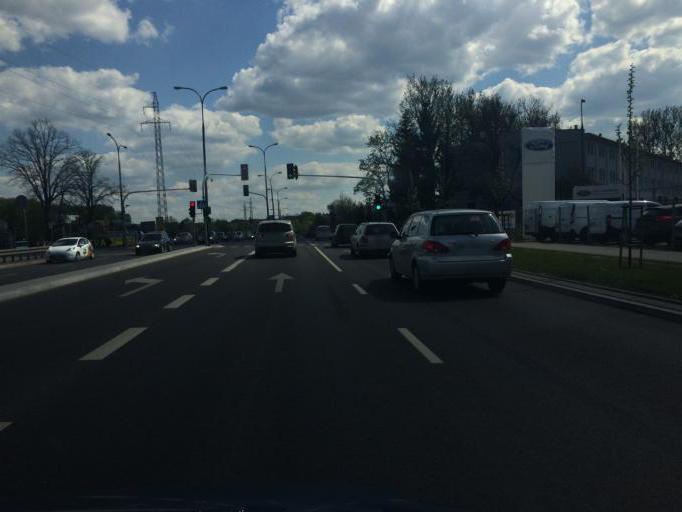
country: PL
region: Warmian-Masurian Voivodeship
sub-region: Olsztyn
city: Kortowo
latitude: 53.7726
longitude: 20.4557
